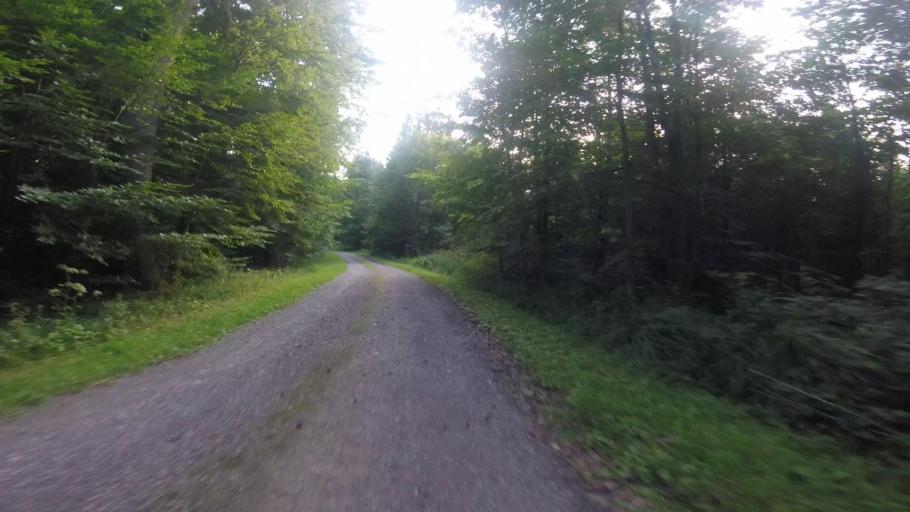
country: DE
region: Baden-Wuerttemberg
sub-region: Regierungsbezirk Stuttgart
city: Kirchberg an der Murr
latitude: 48.9773
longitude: 9.3510
